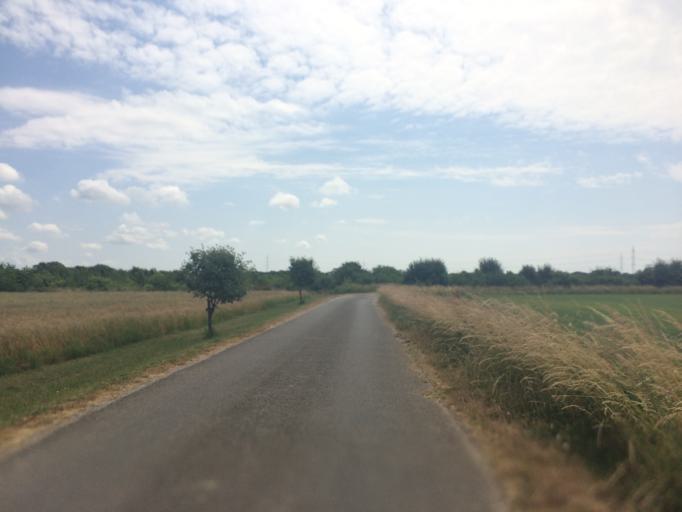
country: DK
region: Capital Region
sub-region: Bornholm Kommune
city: Ronne
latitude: 55.1727
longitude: 14.7264
